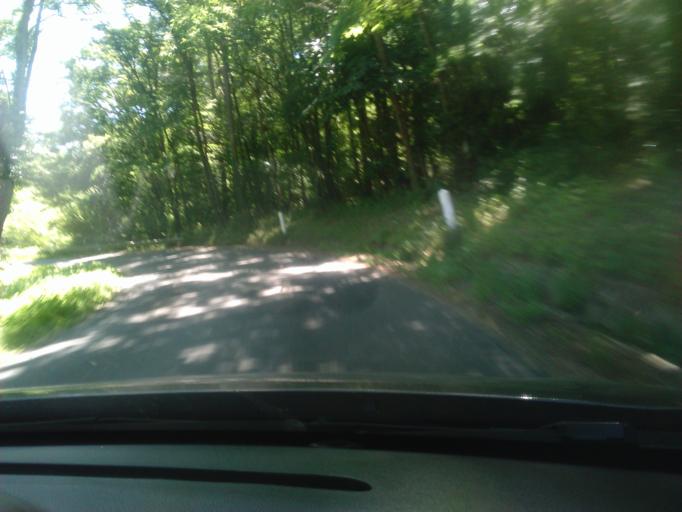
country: FR
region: Centre
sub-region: Departement du Loir-et-Cher
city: Saint-Sulpice-de-Pommeray
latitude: 47.5954
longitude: 1.2111
